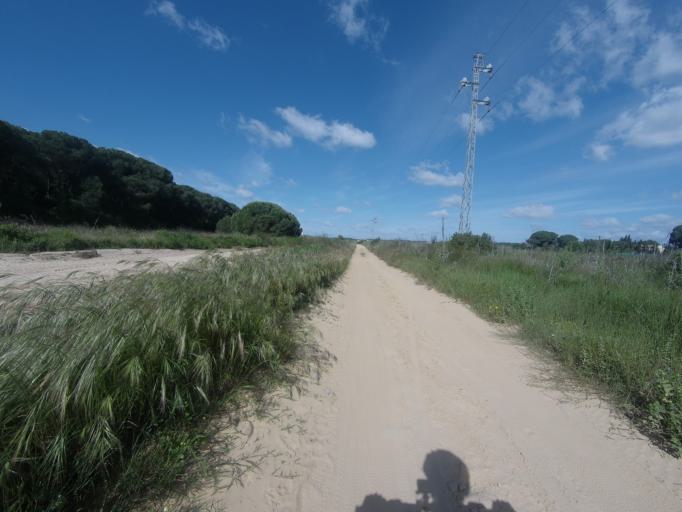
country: ES
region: Andalusia
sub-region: Provincia de Huelva
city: Aljaraque
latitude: 37.2384
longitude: -7.0291
